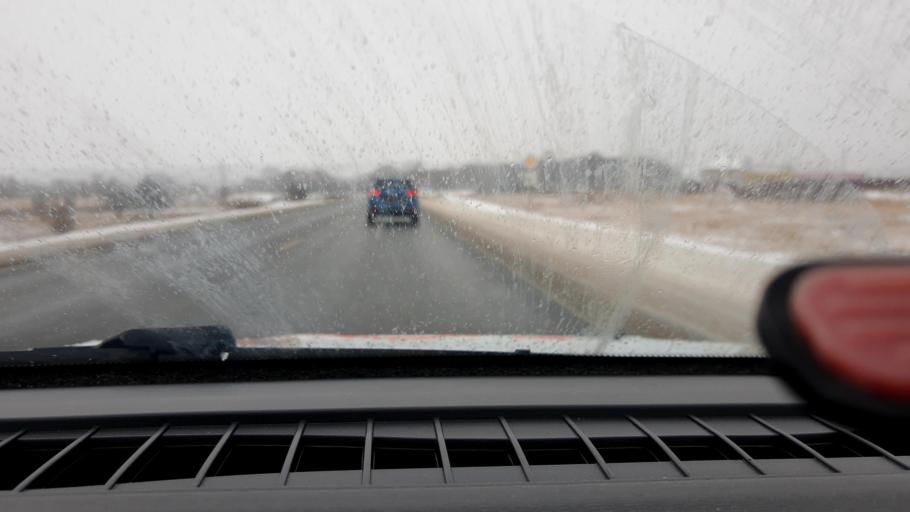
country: RU
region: Nizjnij Novgorod
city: Kstovo
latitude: 56.1138
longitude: 44.1975
